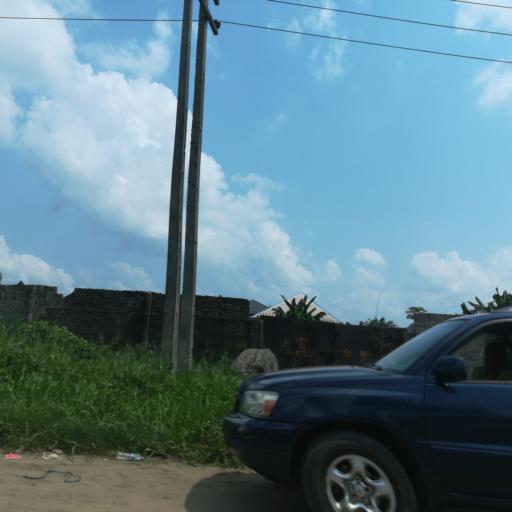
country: NG
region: Rivers
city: Port Harcourt
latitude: 4.8382
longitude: 7.0837
